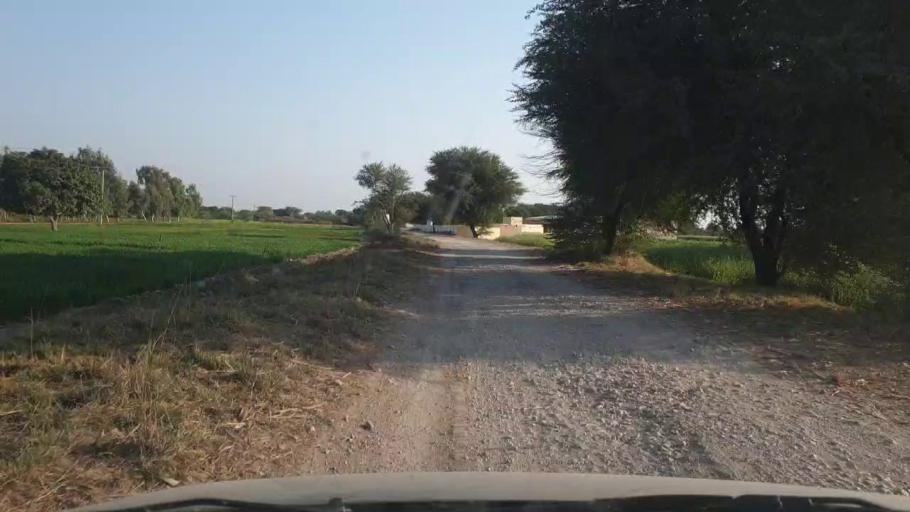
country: PK
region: Sindh
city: Samaro
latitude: 25.2749
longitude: 69.3627
